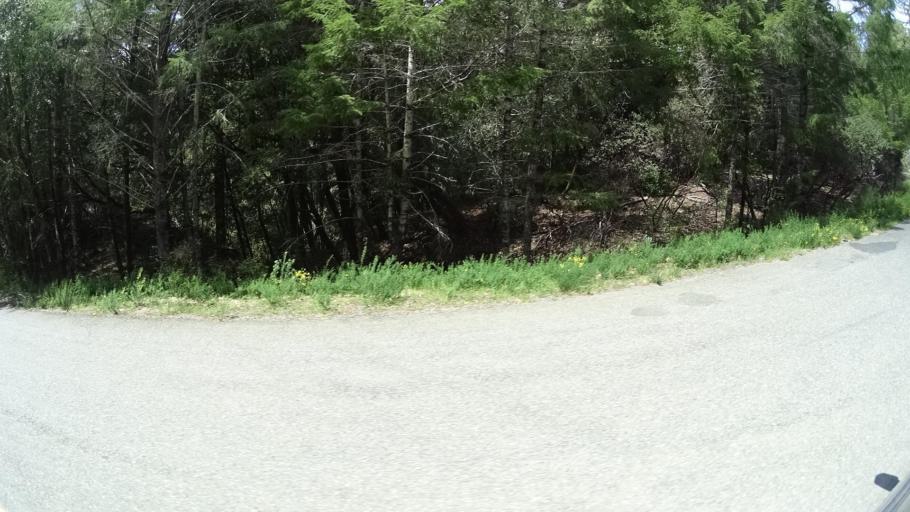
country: US
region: California
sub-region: Humboldt County
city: Redway
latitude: 40.0522
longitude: -123.9558
